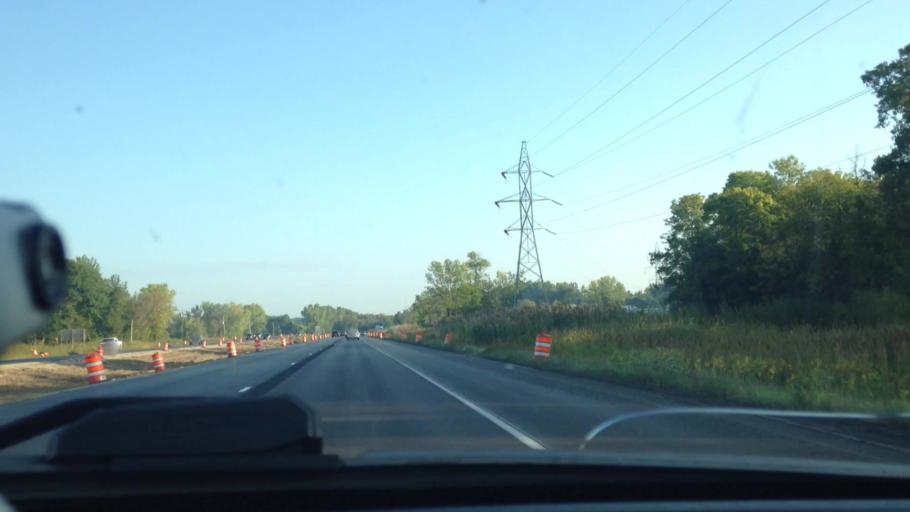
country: US
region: Wisconsin
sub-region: Brown County
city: Suamico
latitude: 44.6233
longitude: -88.0498
